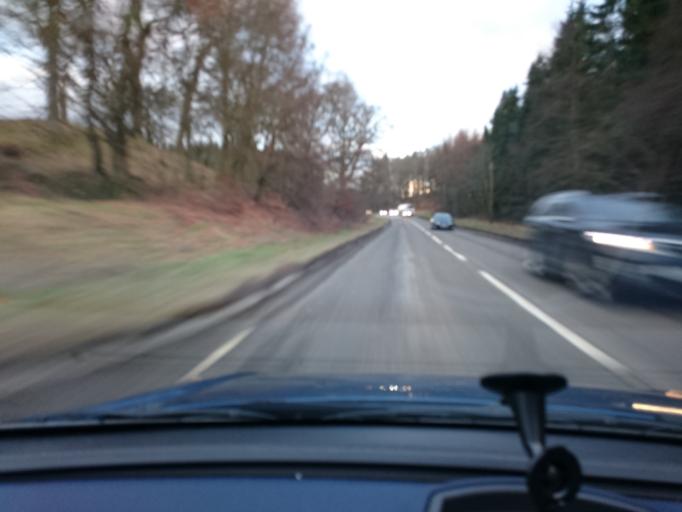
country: GB
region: Scotland
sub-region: Stirling
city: Callander
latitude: 56.2204
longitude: -4.1633
